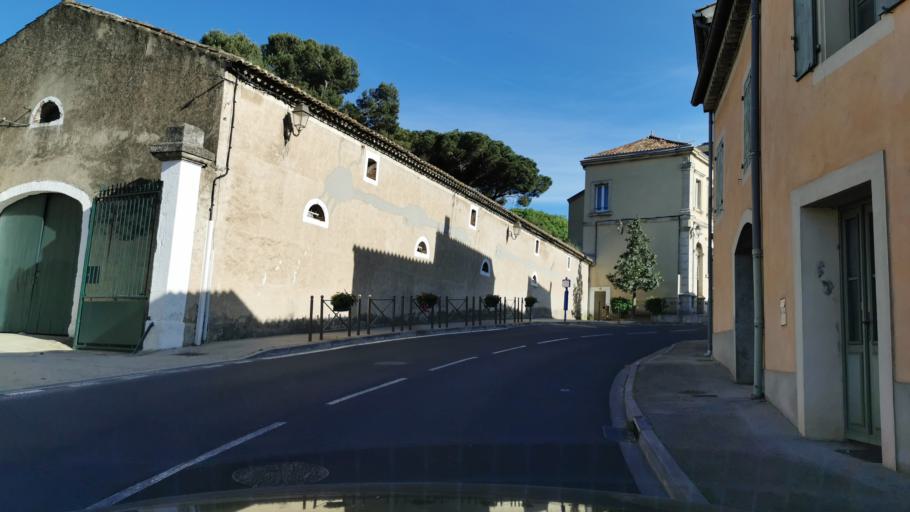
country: FR
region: Languedoc-Roussillon
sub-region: Departement de l'Aude
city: Marcorignan
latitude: 43.2256
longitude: 2.9223
